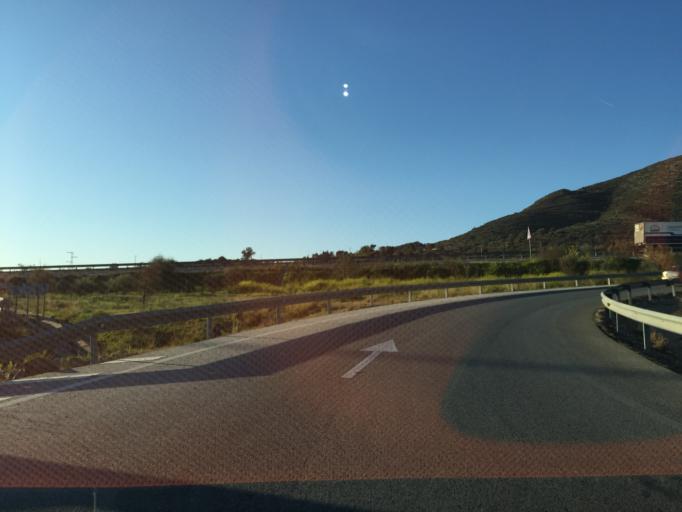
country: ES
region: Andalusia
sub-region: Provincia de Malaga
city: Estacion de Cartama
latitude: 36.7193
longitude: -4.5924
